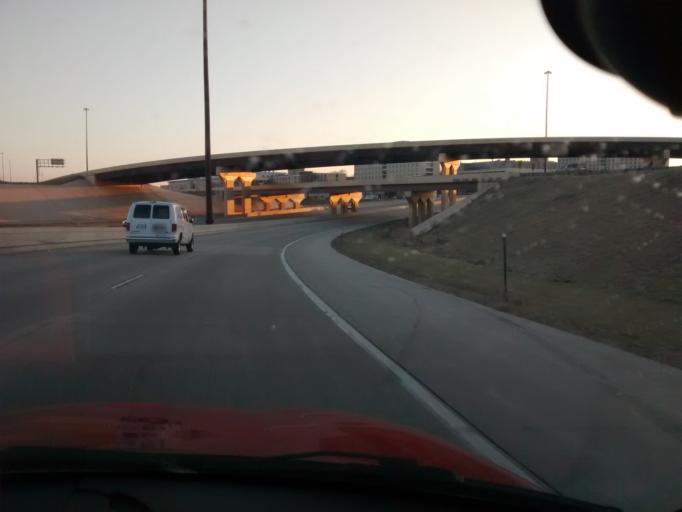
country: US
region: Nebraska
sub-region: Douglas County
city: Omaha
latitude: 41.2615
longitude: -95.9535
